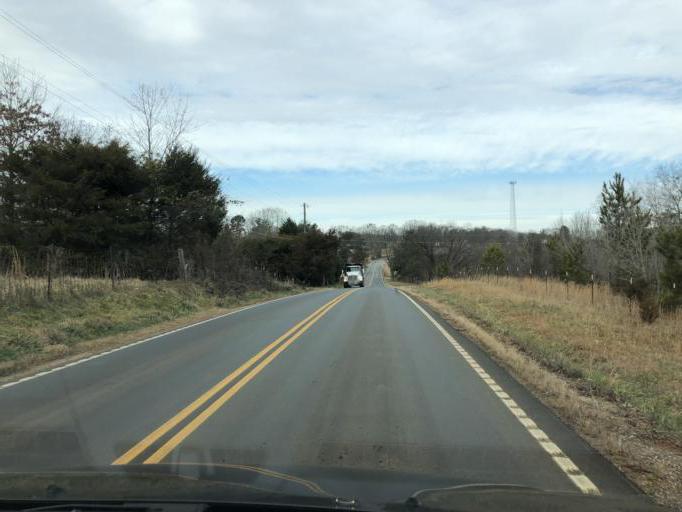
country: US
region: South Carolina
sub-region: Greenville County
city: Five Forks
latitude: 34.8569
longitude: -82.1965
